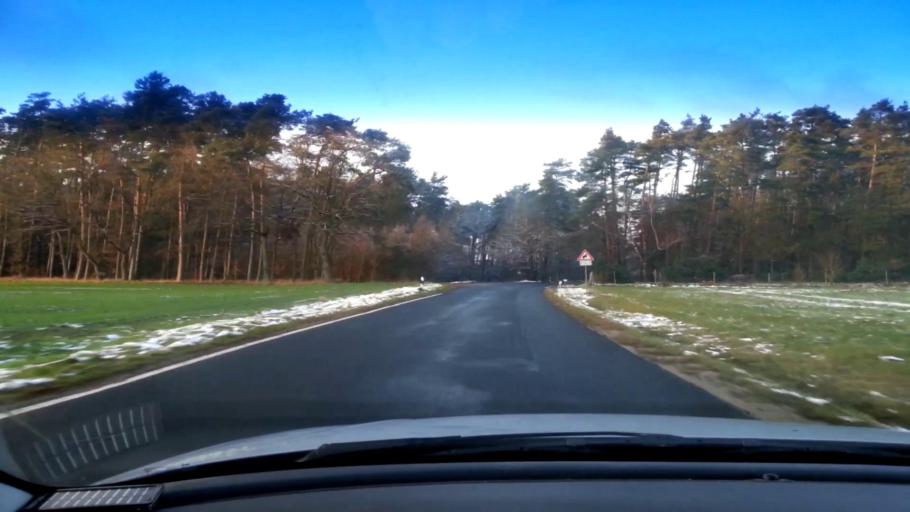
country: DE
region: Bavaria
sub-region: Regierungsbezirk Mittelfranken
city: Adelsdorf
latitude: 49.7644
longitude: 10.8942
